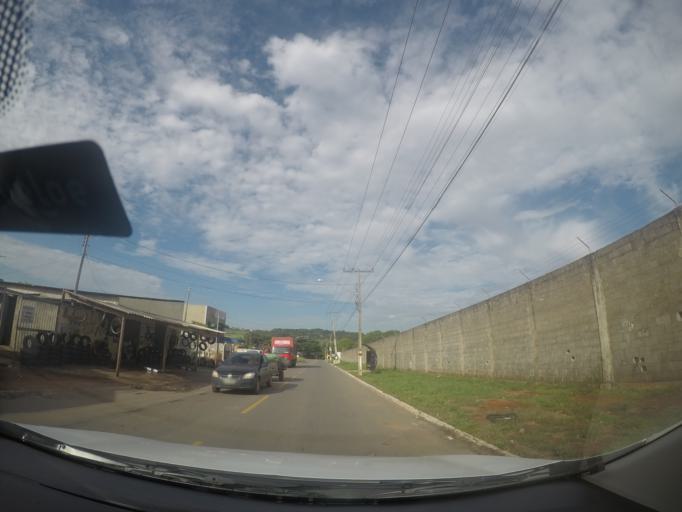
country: BR
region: Goias
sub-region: Goiania
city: Goiania
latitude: -16.6950
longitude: -49.1906
